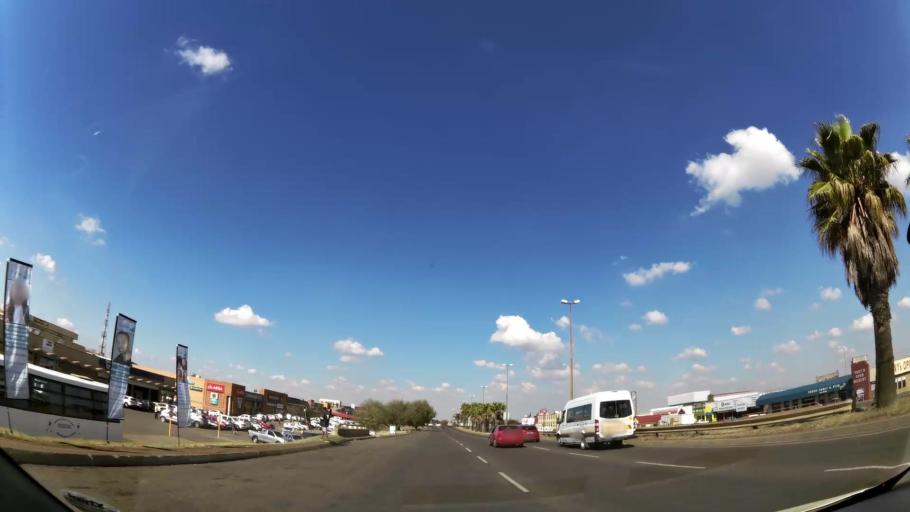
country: ZA
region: Mpumalanga
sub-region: Nkangala District Municipality
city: Witbank
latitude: -25.9001
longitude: 29.2331
